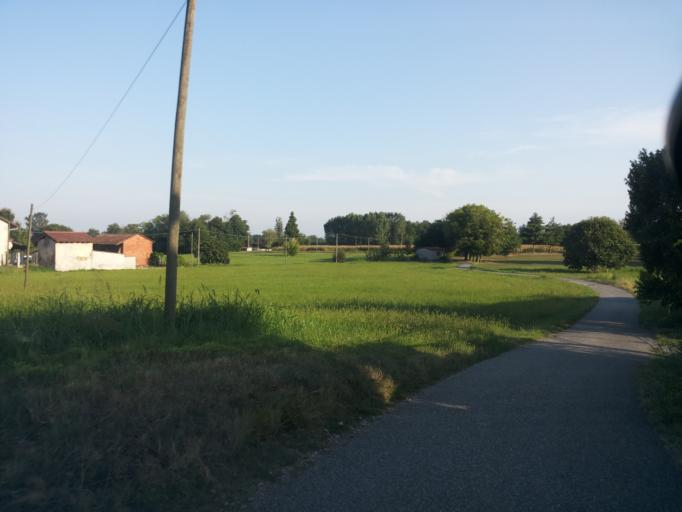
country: IT
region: Piedmont
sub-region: Provincia di Biella
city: Cavaglia
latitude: 45.3962
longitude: 8.1101
